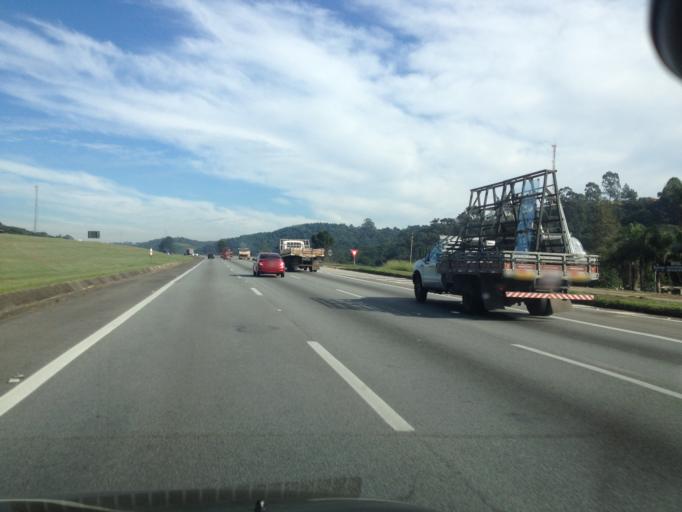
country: BR
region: Sao Paulo
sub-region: Mairinque
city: Mairinque
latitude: -23.4185
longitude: -47.2137
